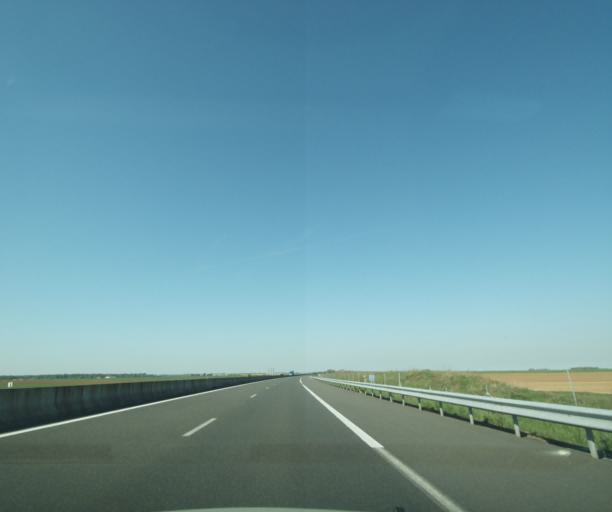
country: FR
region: Centre
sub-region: Departement du Loiret
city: Artenay
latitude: 48.0509
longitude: 1.9280
